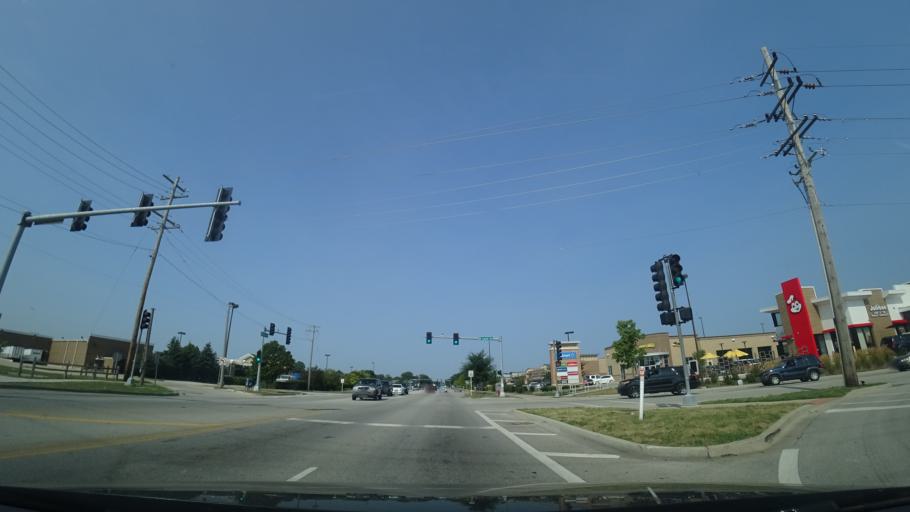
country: US
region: Illinois
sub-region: Cook County
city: Lincolnwood
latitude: 42.0119
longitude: -87.7173
